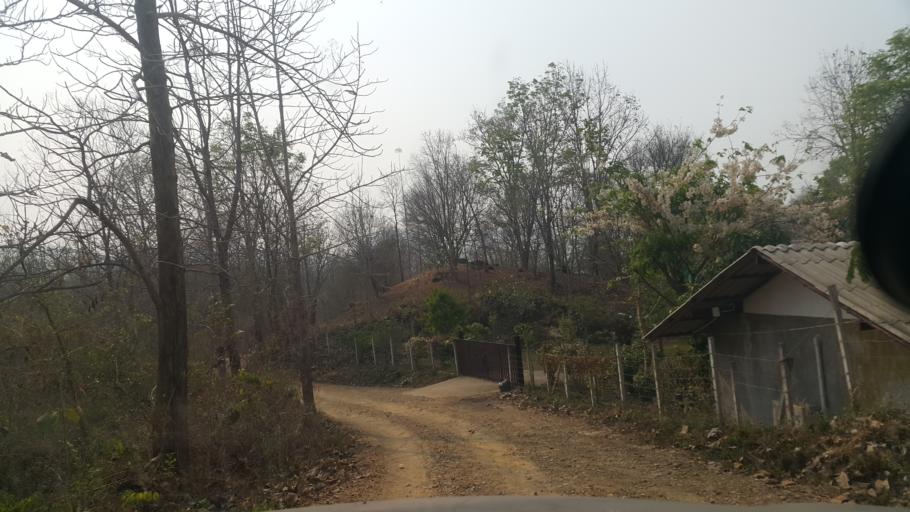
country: TH
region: Chiang Mai
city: Mae On
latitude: 18.7755
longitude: 99.2662
